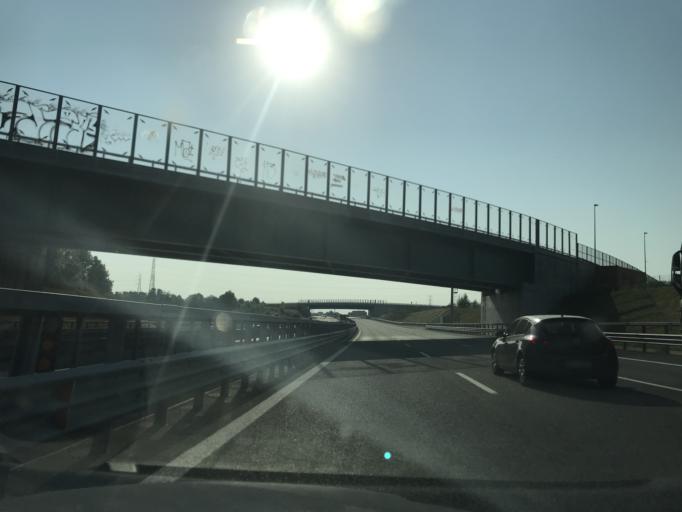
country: IT
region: Lombardy
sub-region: Citta metropolitana di Milano
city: Albignano
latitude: 45.5056
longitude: 9.4914
